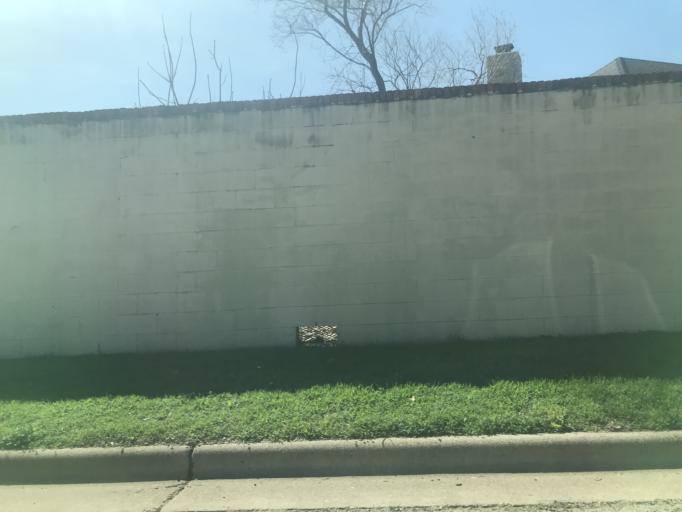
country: US
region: Texas
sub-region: Taylor County
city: Abilene
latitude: 32.4491
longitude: -99.7665
